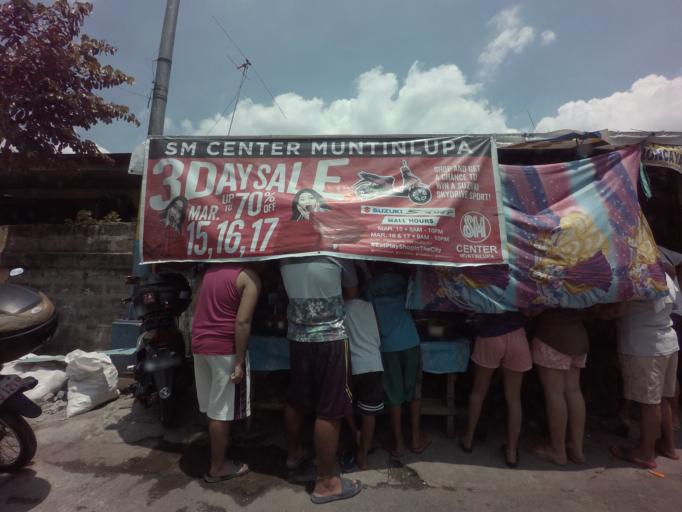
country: PH
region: Calabarzon
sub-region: Province of Laguna
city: San Pedro
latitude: 14.3892
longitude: 121.0499
